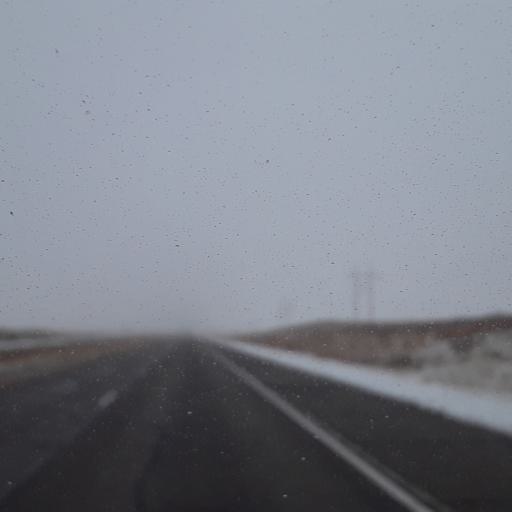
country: US
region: Colorado
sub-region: Logan County
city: Sterling
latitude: 40.7894
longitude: -102.8936
